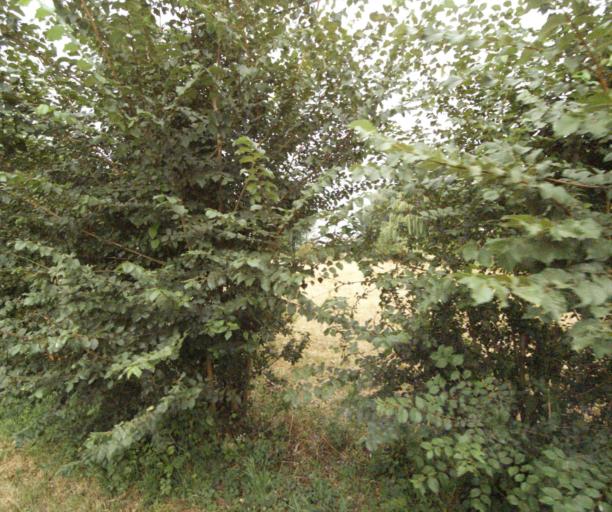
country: FR
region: Nord-Pas-de-Calais
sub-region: Departement du Nord
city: Bondues
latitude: 50.6991
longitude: 3.0803
